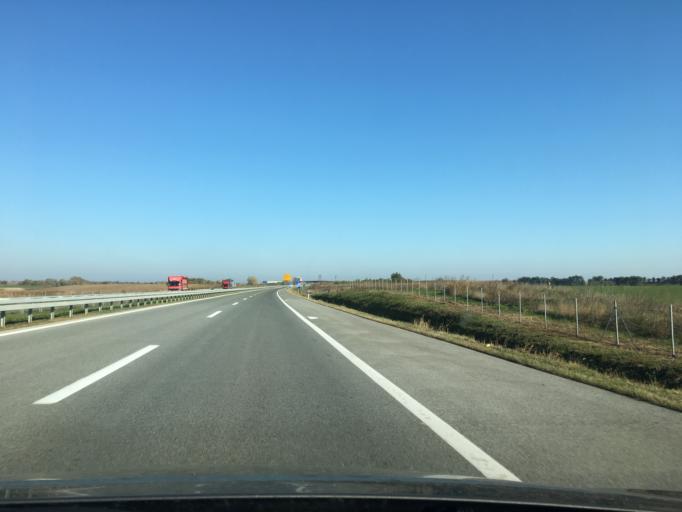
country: RS
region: Autonomna Pokrajina Vojvodina
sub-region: Severnobacki Okrug
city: Mali Igos
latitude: 45.6339
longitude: 19.7092
